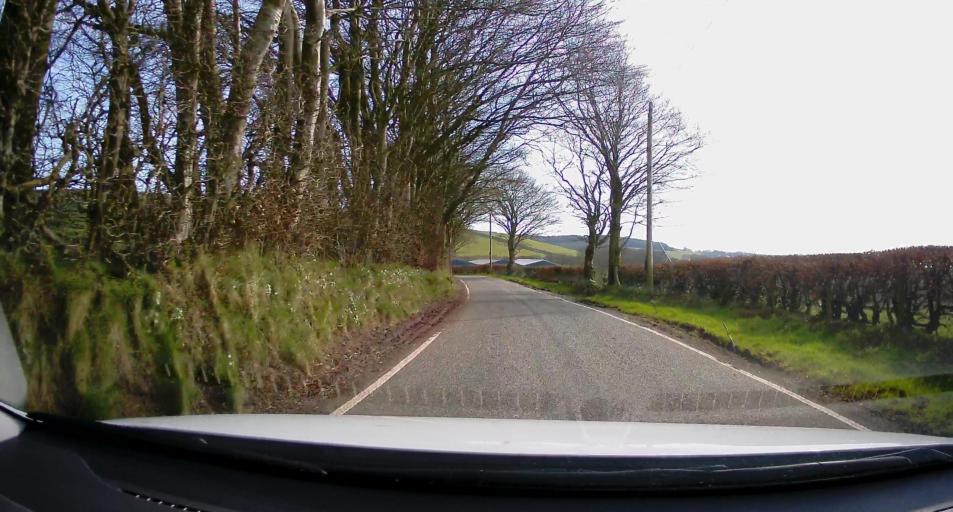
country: GB
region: Wales
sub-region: County of Ceredigion
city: Lledrod
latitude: 52.2723
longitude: -4.0692
